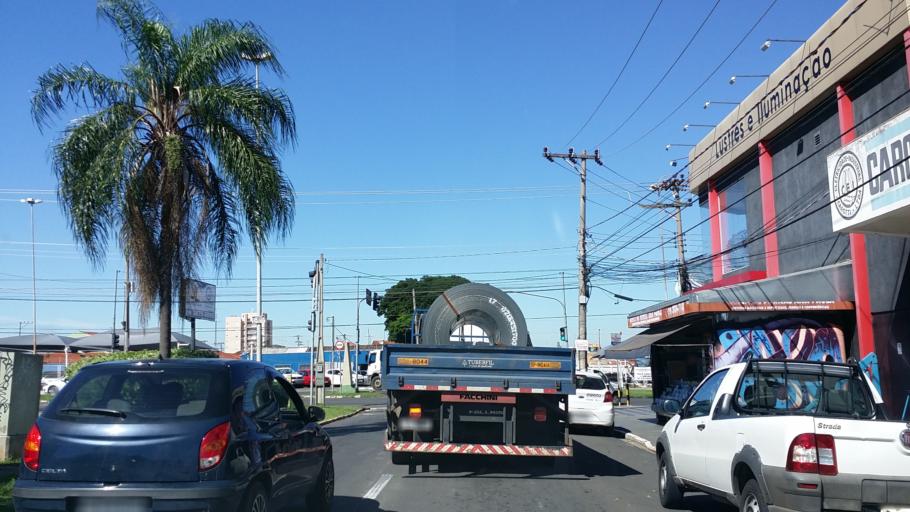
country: BR
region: Sao Paulo
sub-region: Indaiatuba
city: Indaiatuba
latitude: -23.0912
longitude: -47.1960
